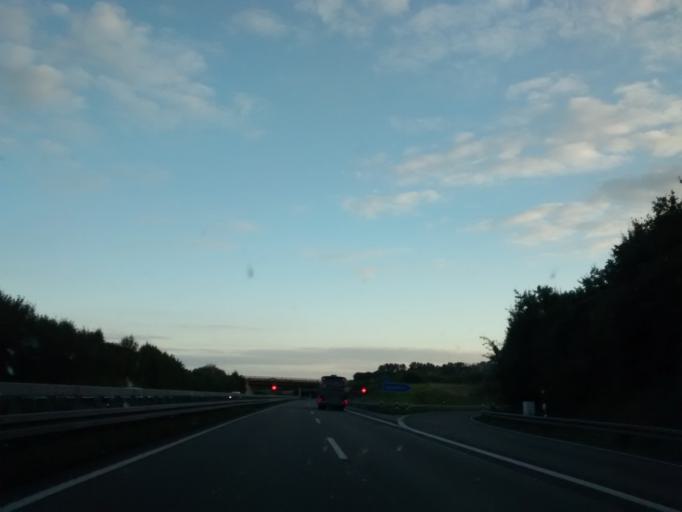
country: DE
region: Lower Saxony
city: Bad Rothenfelde
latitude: 52.1203
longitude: 8.1790
